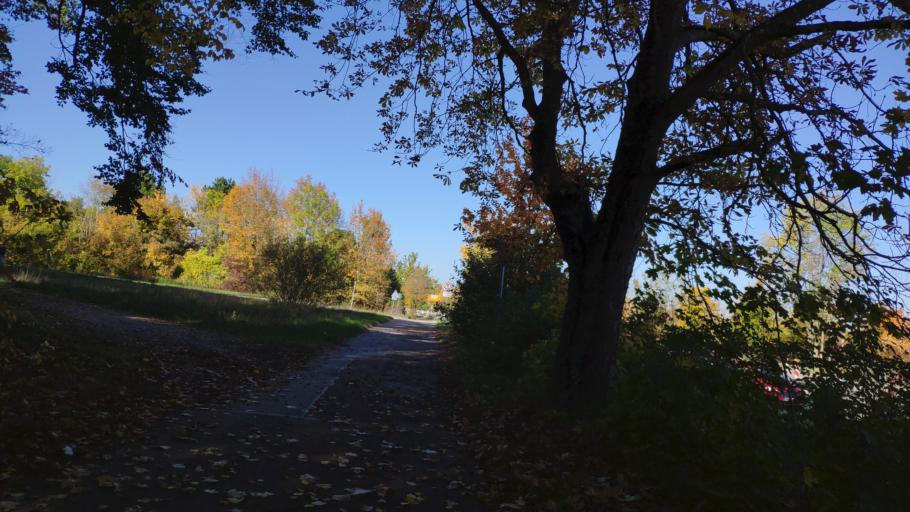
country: DE
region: Baden-Wuerttemberg
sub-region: Tuebingen Region
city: Ulm
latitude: 48.4207
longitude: 9.9831
